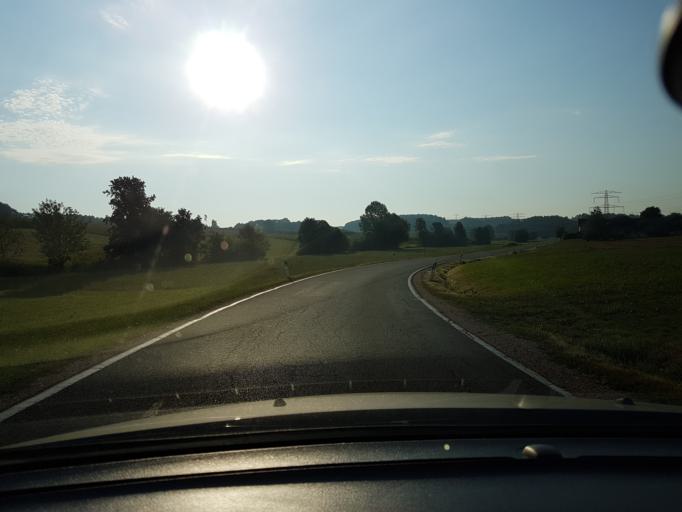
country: DE
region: Bavaria
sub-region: Upper Bavaria
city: Egglkofen
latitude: 48.4164
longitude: 12.4861
